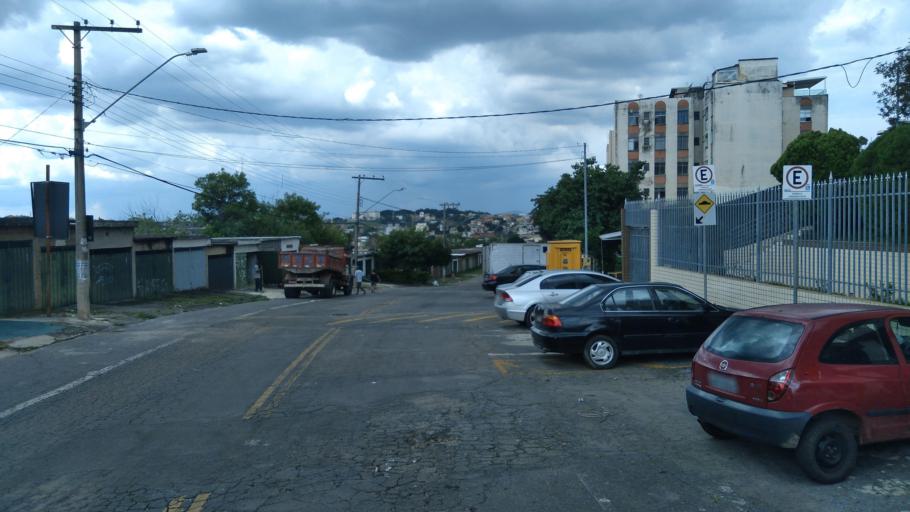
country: BR
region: Minas Gerais
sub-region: Contagem
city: Contagem
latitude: -19.9186
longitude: -44.0110
